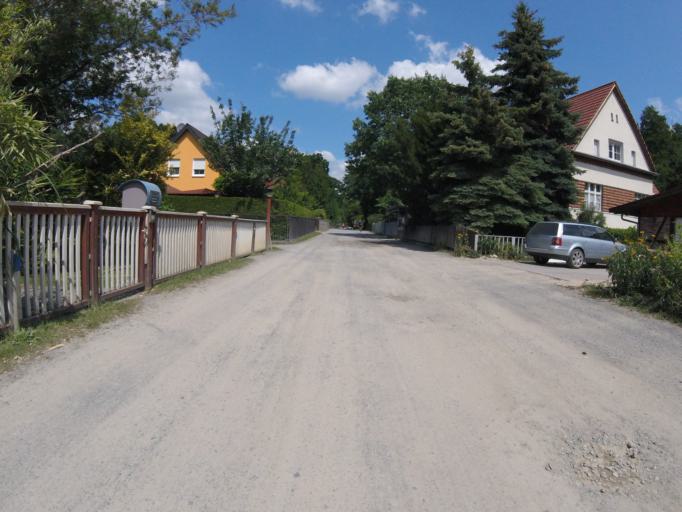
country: DE
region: Brandenburg
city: Bestensee
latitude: 52.2558
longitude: 13.6467
